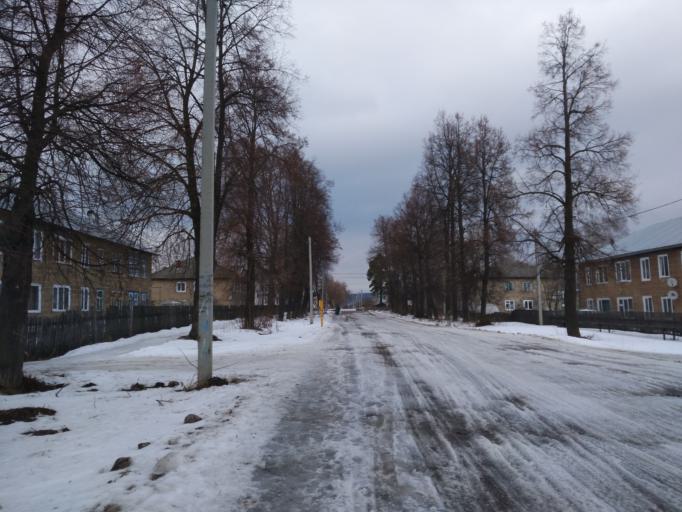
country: RU
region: Kirov
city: Krasnaya Polyana
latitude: 56.2401
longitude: 51.1411
